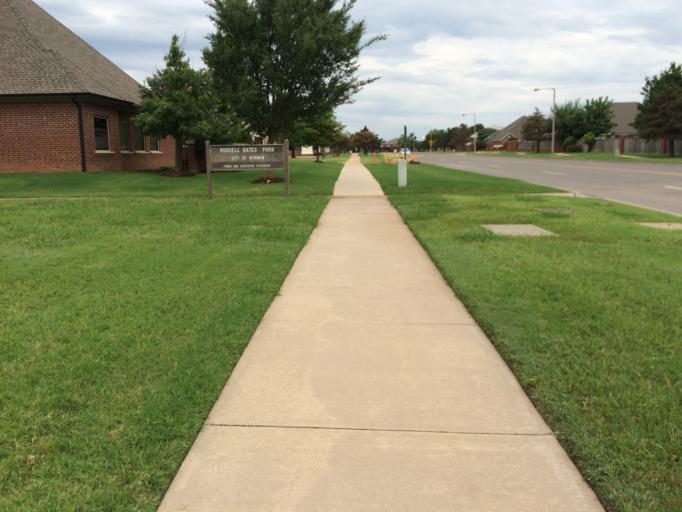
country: US
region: Oklahoma
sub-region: Cleveland County
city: Norman
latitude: 35.2272
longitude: -97.4783
